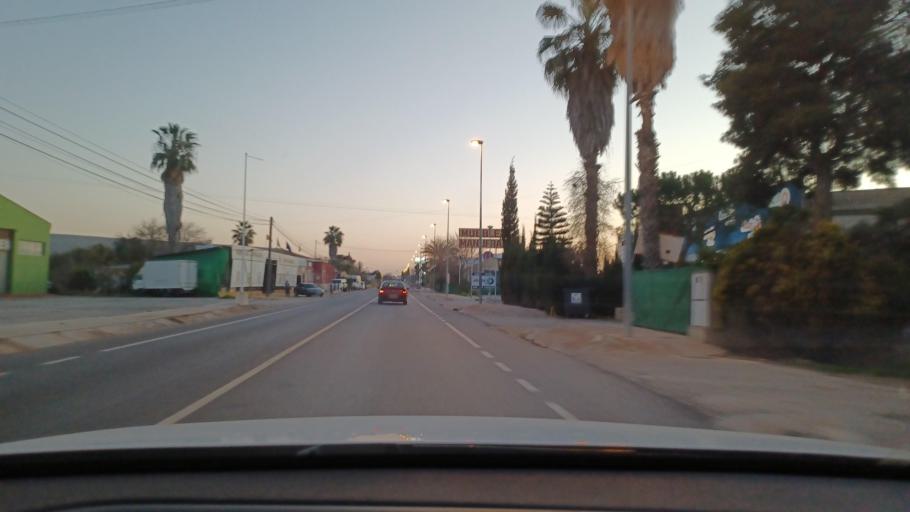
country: ES
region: Valencia
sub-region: Provincia de Alicante
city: Dolores
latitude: 38.1346
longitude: -0.7732
